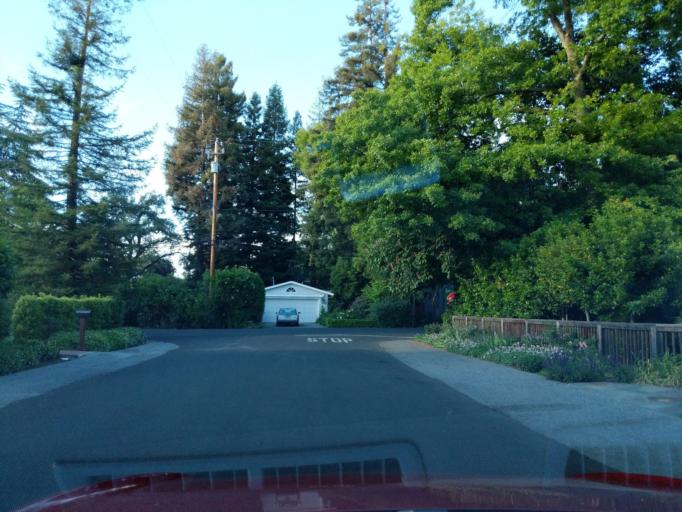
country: US
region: California
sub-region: San Mateo County
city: Menlo Park
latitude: 37.4406
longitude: -122.1825
